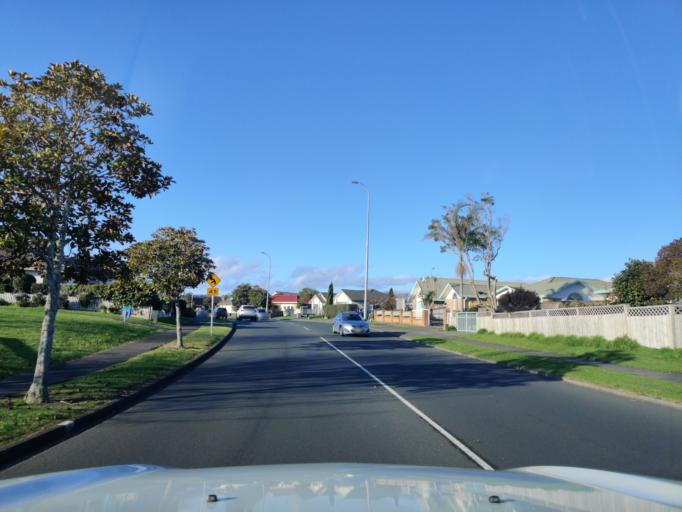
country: NZ
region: Auckland
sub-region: Auckland
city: Pakuranga
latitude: -36.9199
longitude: 174.9160
